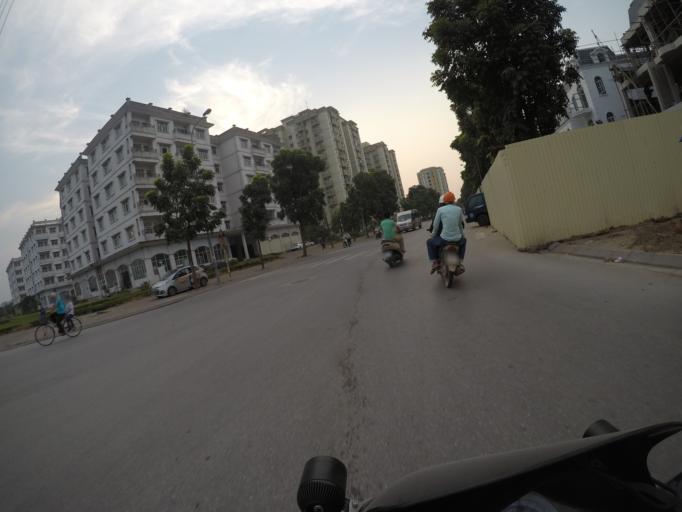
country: VN
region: Ha Noi
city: Trau Quy
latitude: 21.0392
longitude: 105.9076
